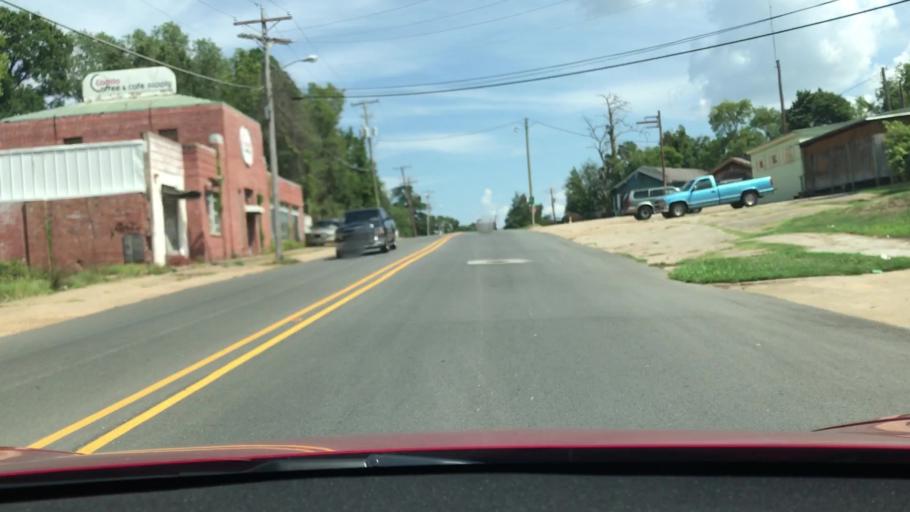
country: US
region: Louisiana
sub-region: Bossier Parish
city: Bossier City
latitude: 32.5024
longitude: -93.7353
